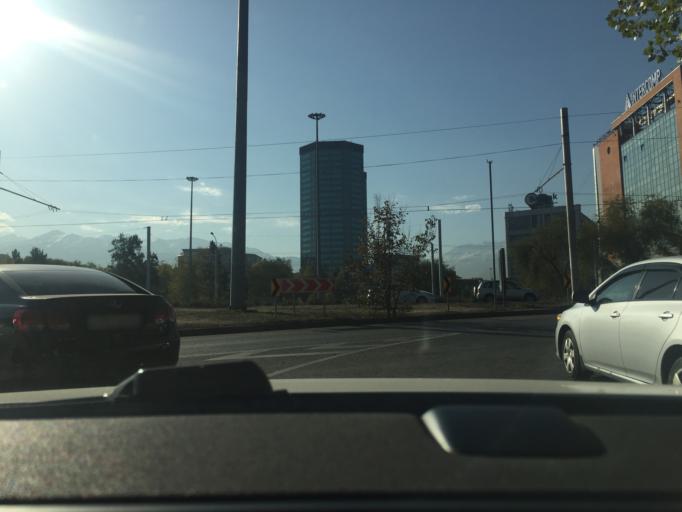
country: KZ
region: Almaty Qalasy
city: Almaty
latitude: 43.2408
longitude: 76.9147
